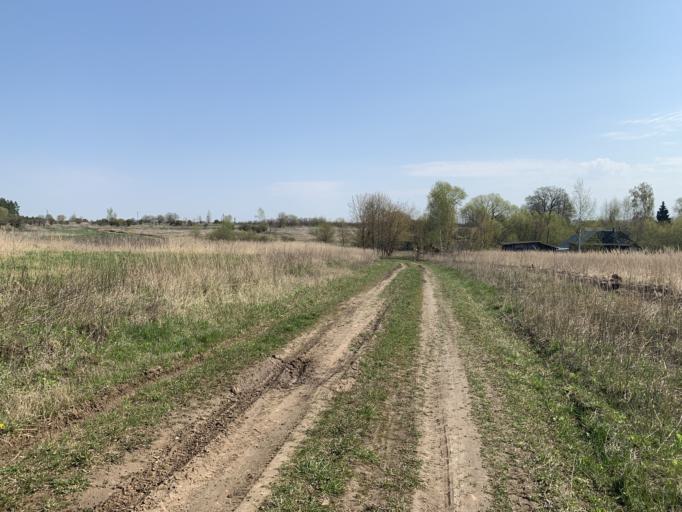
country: RU
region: Tula
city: Belev
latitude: 53.7863
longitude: 36.0720
